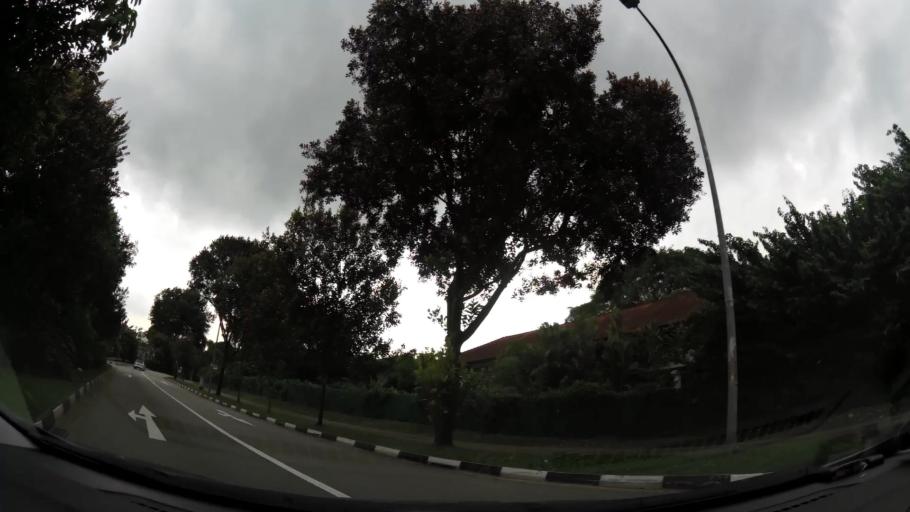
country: MY
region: Johor
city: Kampung Pasir Gudang Baru
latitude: 1.4578
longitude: 103.8358
